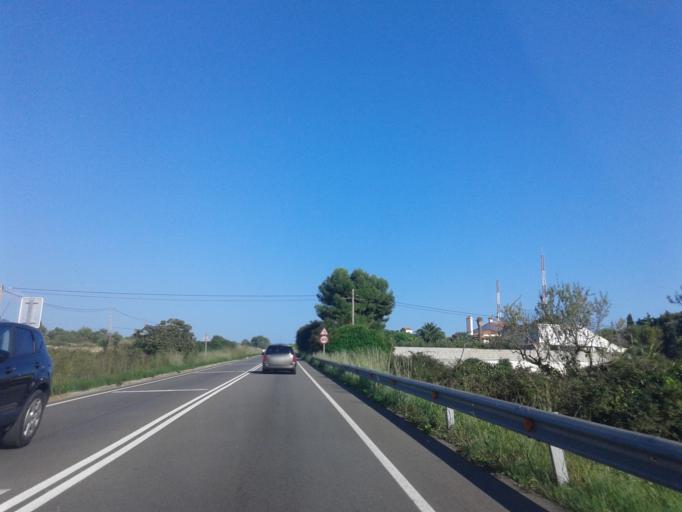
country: ES
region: Catalonia
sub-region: Provincia de Barcelona
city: Vilanova i la Geltru
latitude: 41.2111
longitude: 1.7036
